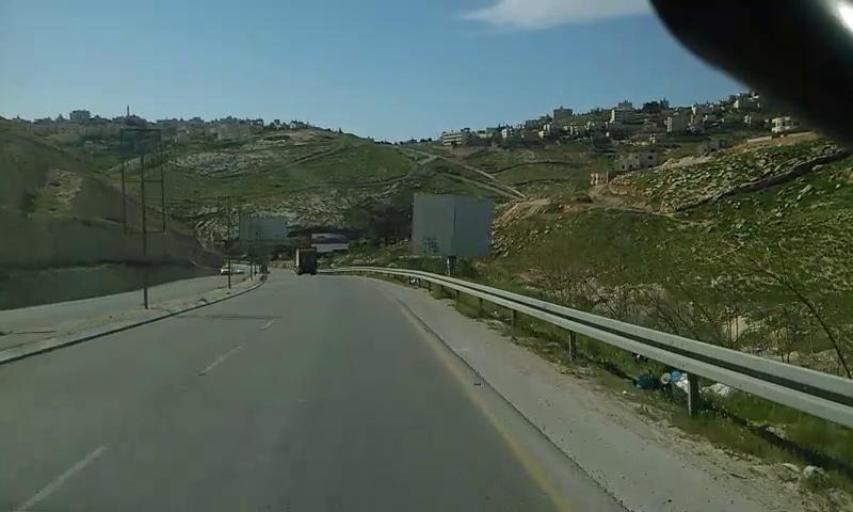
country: PS
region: West Bank
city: Abu Dis
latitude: 31.7475
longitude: 35.2796
